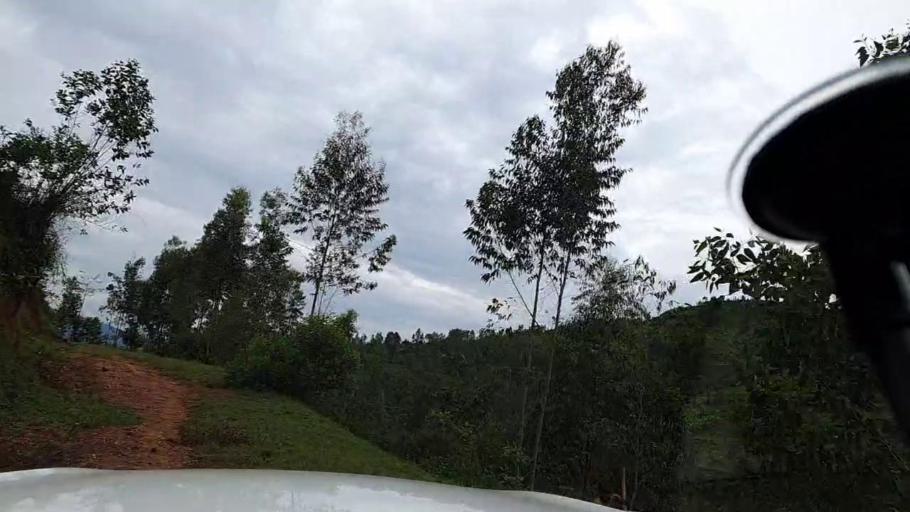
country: RW
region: Southern Province
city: Gitarama
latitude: -2.0847
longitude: 29.6489
